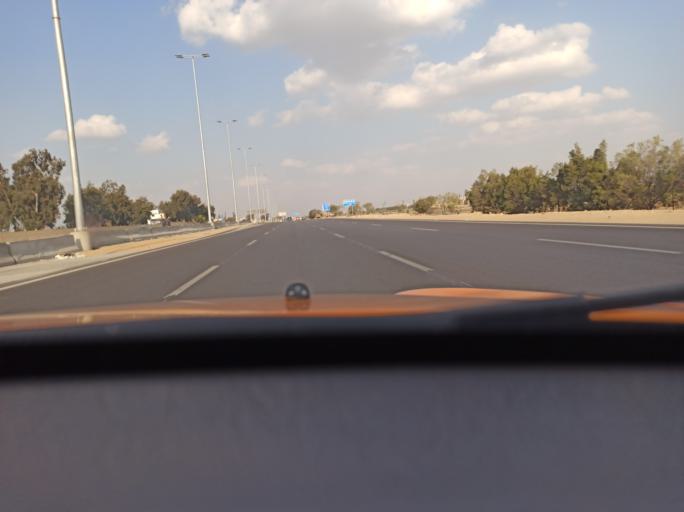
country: EG
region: Al Isma'iliyah
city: Ismailia
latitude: 30.6182
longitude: 32.2323
